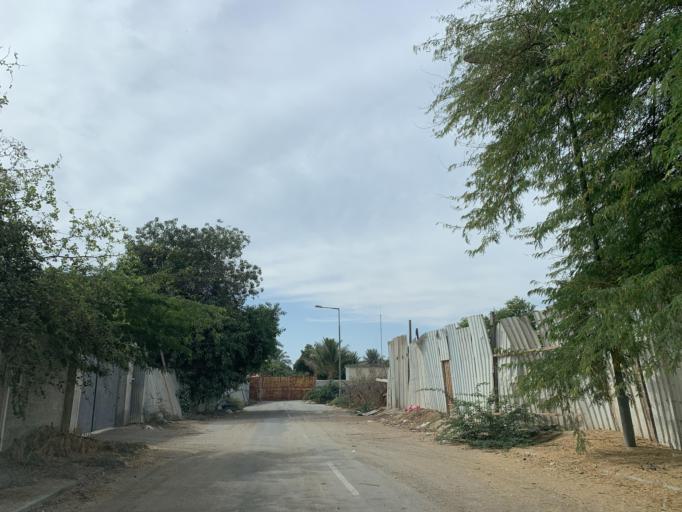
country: BH
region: Central Governorate
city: Madinat Hamad
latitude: 26.1152
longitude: 50.4719
